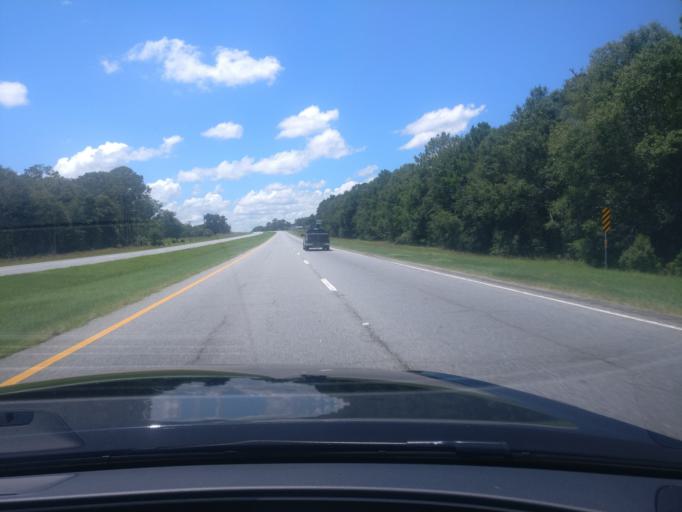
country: US
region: Georgia
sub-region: Tift County
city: Omega
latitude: 31.4757
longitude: -83.6714
